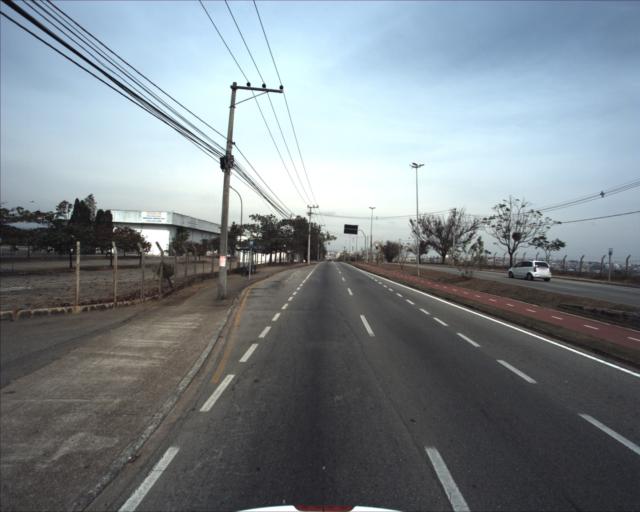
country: BR
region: Sao Paulo
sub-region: Sorocaba
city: Sorocaba
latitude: -23.4586
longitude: -47.4518
